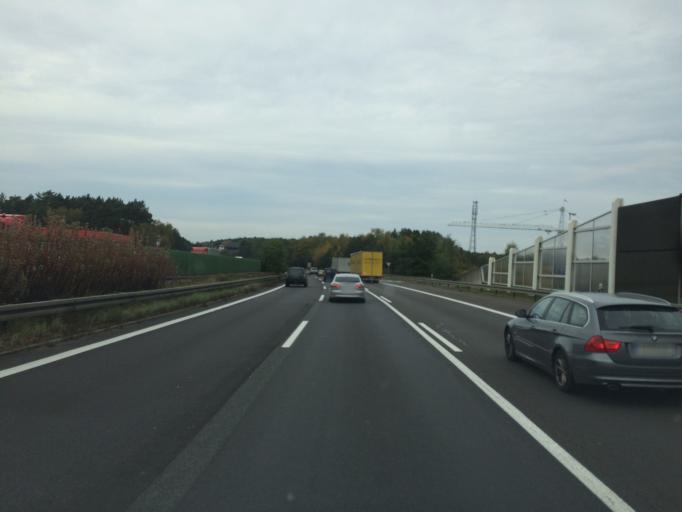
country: DE
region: Brandenburg
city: Michendorf
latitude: 52.3028
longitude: 13.0160
